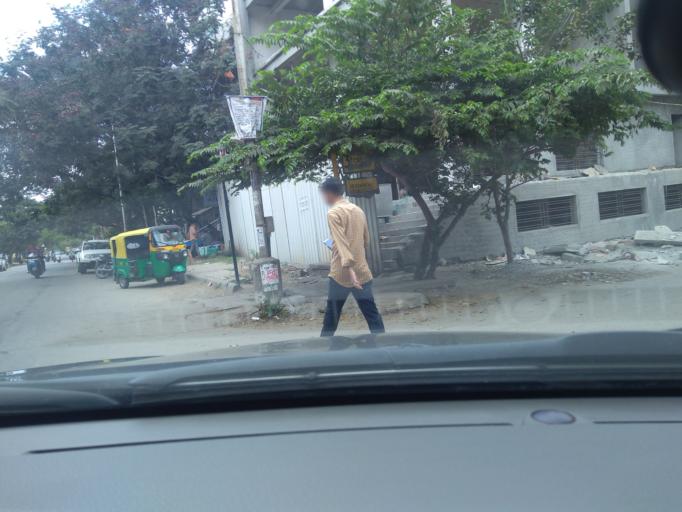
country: IN
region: Karnataka
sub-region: Bangalore Urban
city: Bangalore
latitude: 13.0045
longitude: 77.6602
